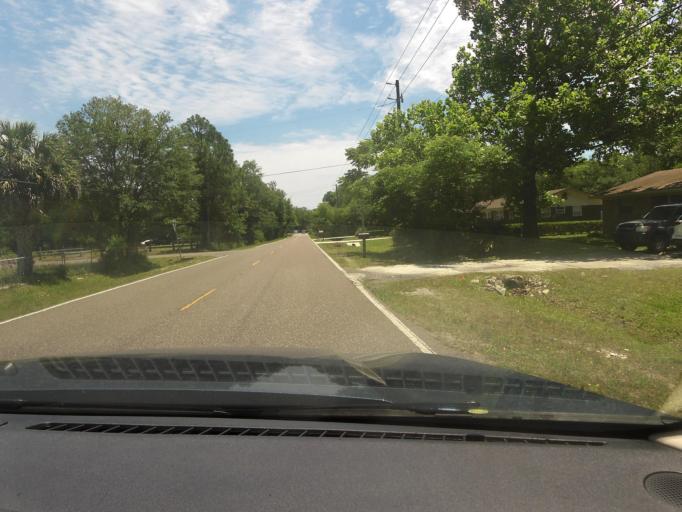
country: US
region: Florida
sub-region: Duval County
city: Jacksonville
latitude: 30.4600
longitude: -81.5359
